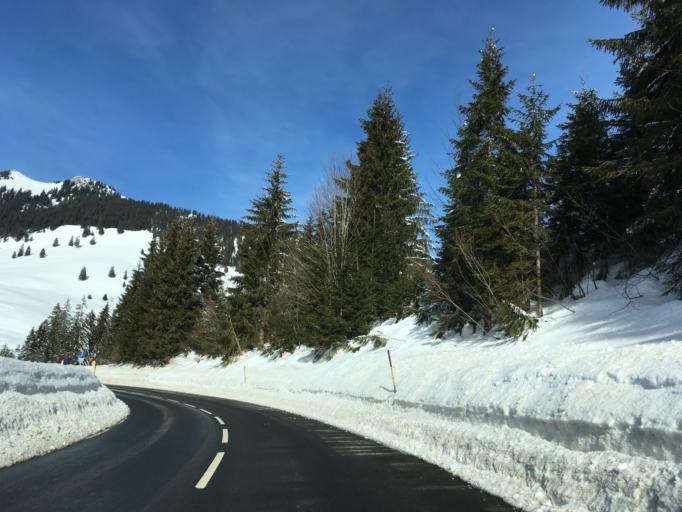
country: DE
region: Bavaria
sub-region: Upper Bavaria
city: Bayrischzell
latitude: 47.6858
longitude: 12.0574
